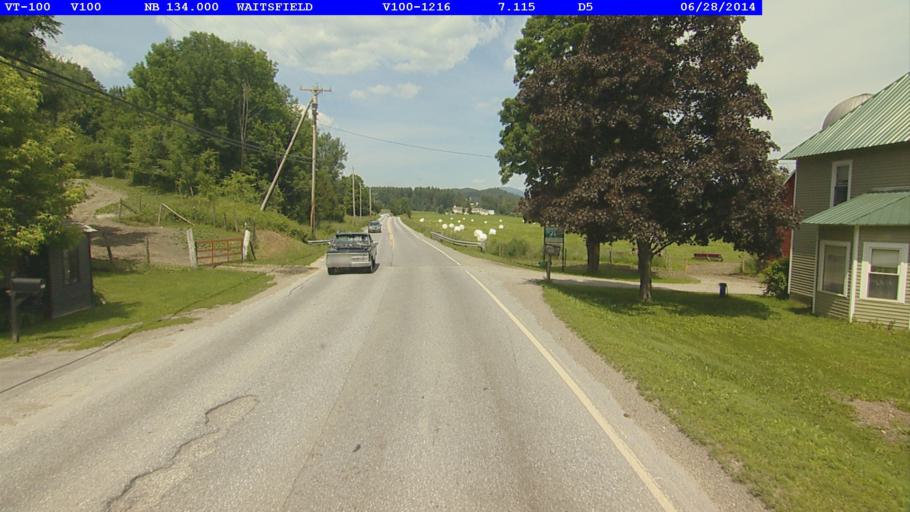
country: US
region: Vermont
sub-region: Washington County
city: Waterbury
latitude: 44.2290
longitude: -72.7839
